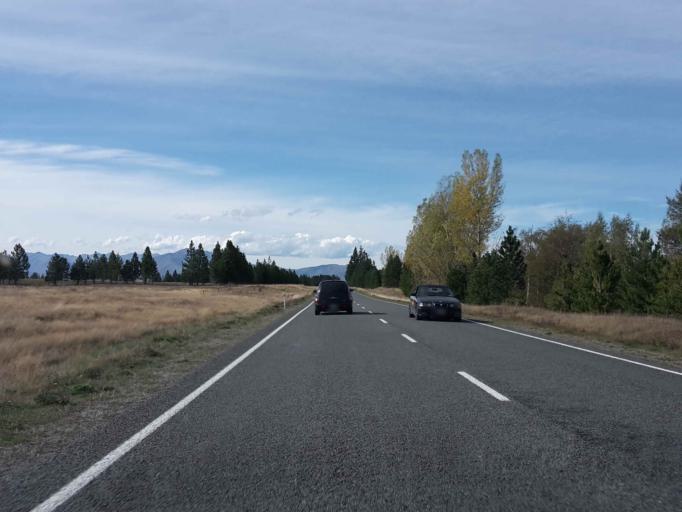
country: NZ
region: Canterbury
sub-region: Timaru District
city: Pleasant Point
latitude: -44.1876
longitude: 170.3013
